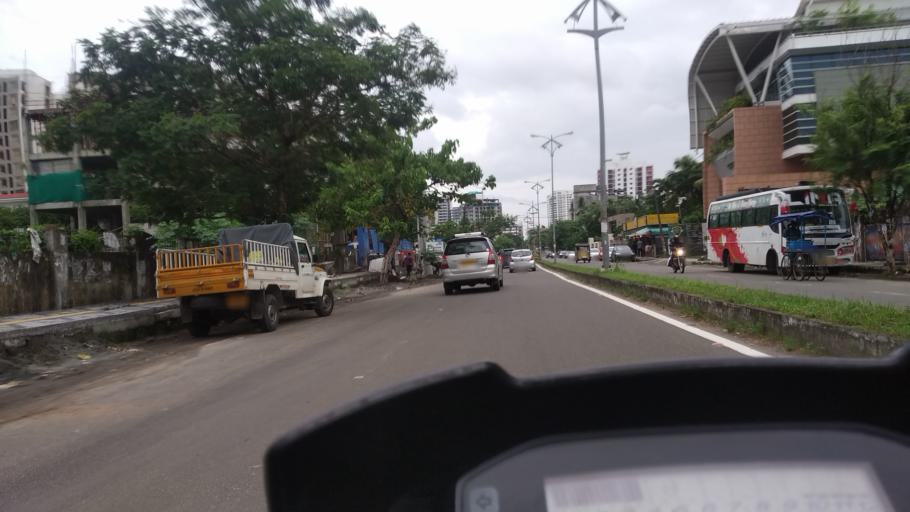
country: IN
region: Kerala
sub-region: Ernakulam
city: Cochin
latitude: 9.9950
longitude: 76.3015
